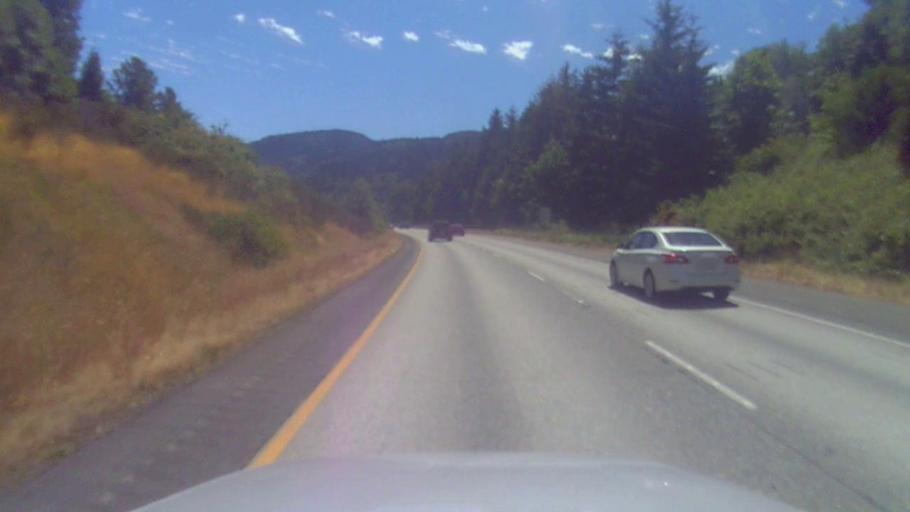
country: US
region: Washington
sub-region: Whatcom County
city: Bellingham
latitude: 48.7047
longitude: -122.4765
